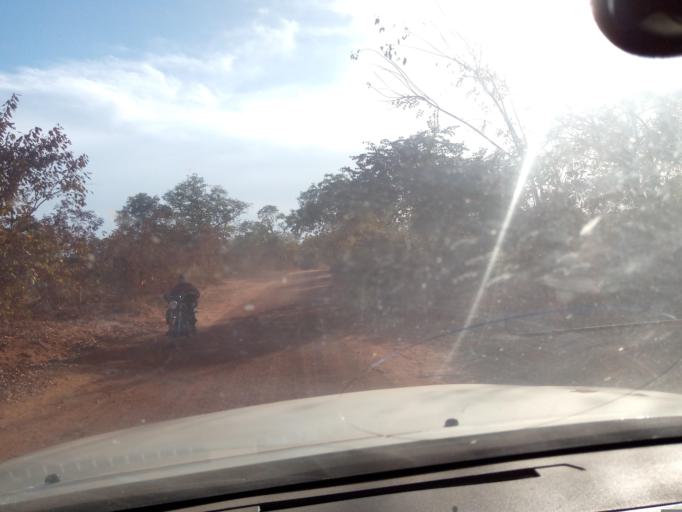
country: ML
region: Sikasso
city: Sikasso
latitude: 11.4211
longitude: -5.5638
